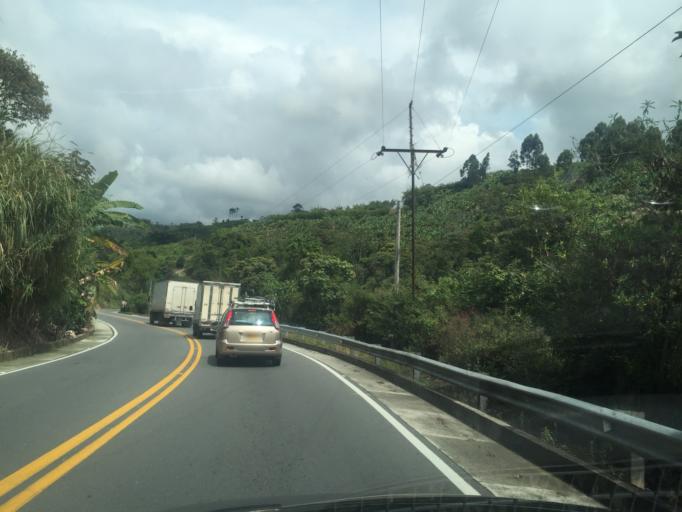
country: CO
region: Caldas
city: Villamaria
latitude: 5.0153
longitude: -75.5445
